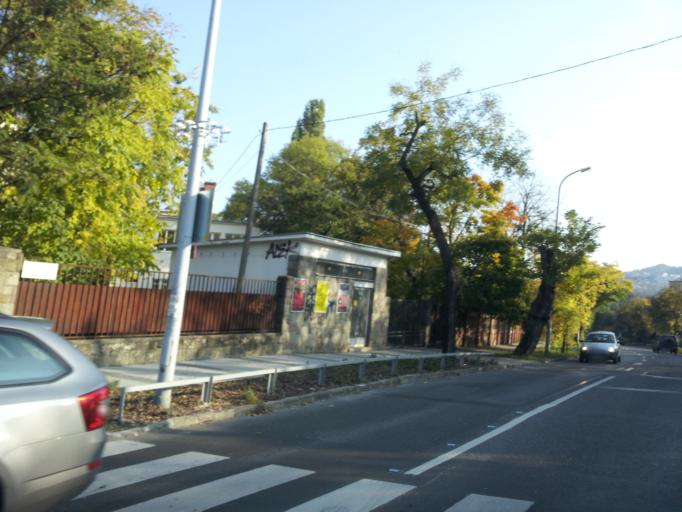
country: HU
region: Budapest
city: Budapest XII. keruelet
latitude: 47.4929
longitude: 19.0121
